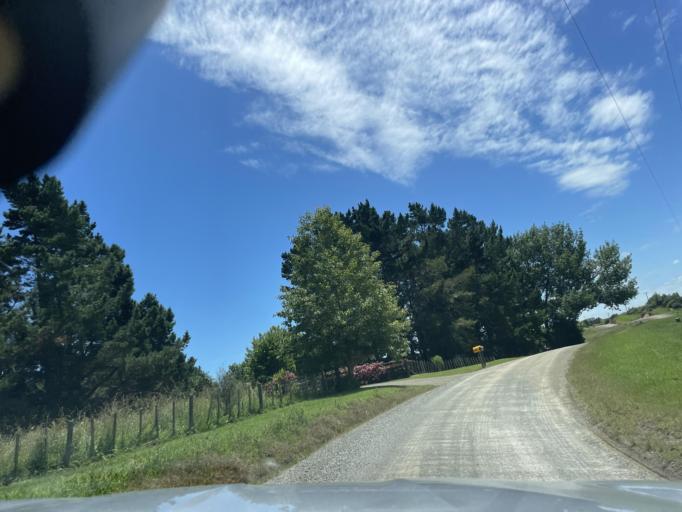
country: NZ
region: Auckland
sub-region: Auckland
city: Wellsford
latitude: -36.2250
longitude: 174.3653
